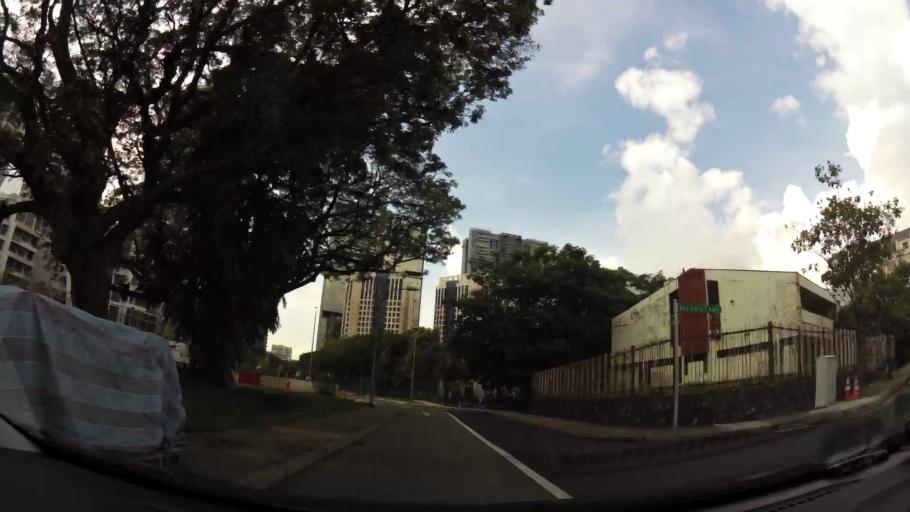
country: SG
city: Singapore
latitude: 1.2941
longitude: 103.8189
